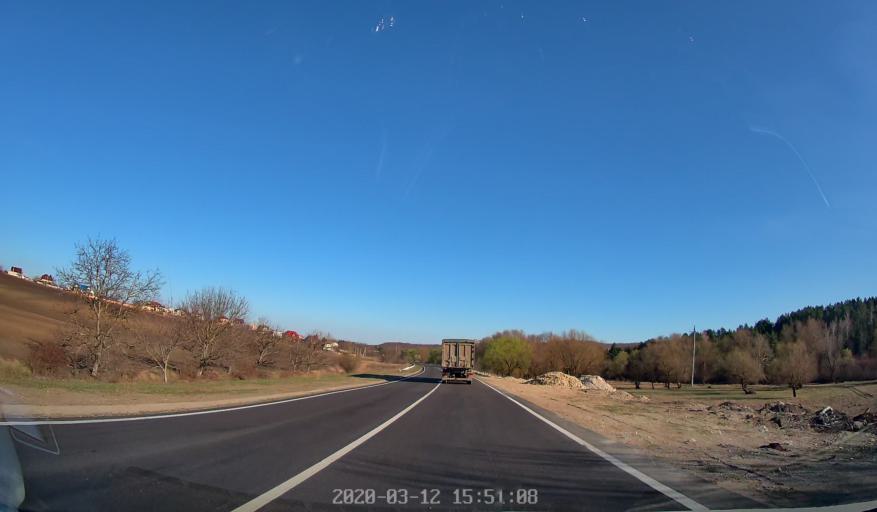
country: MD
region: Chisinau
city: Ciorescu
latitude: 47.0685
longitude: 28.9634
